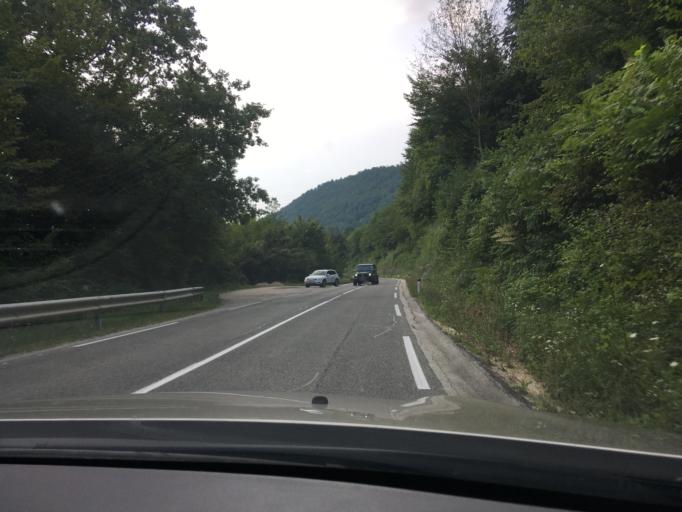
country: SI
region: Zuzemberk
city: Zuzemberk
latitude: 45.7906
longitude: 14.9890
